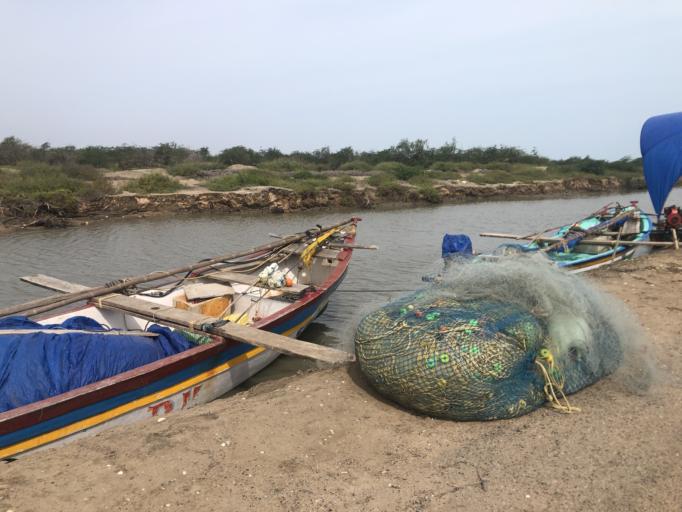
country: IN
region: Tamil Nadu
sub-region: Thanjavur
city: Adirampattinam
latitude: 10.3186
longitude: 79.3809
